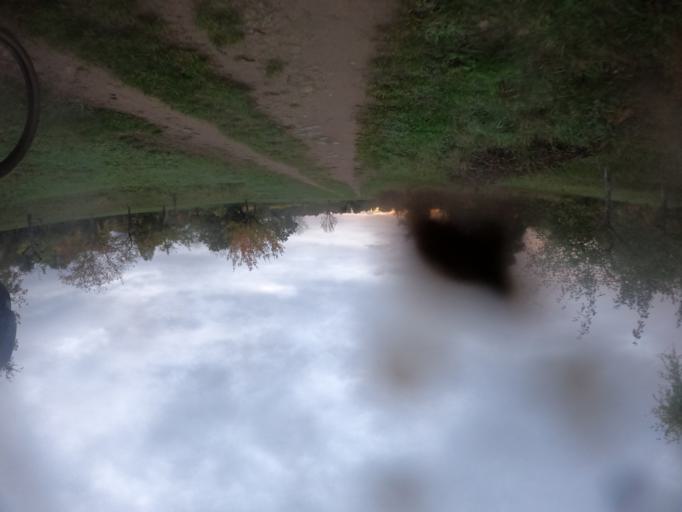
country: DE
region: Hesse
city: Dreieich
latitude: 49.9948
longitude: 8.7167
